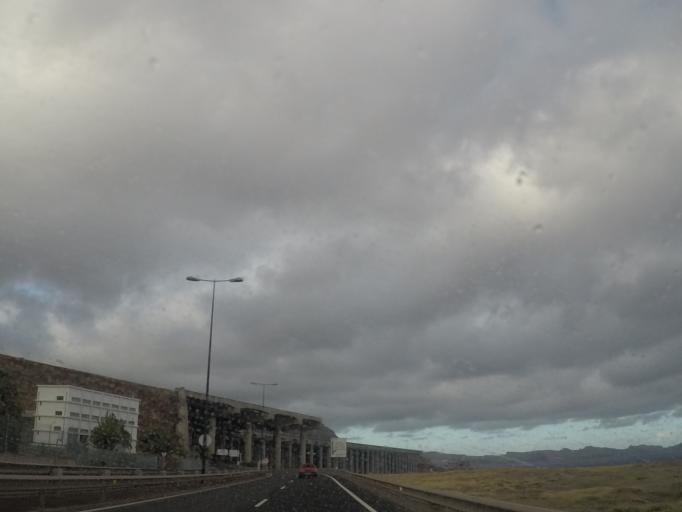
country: PT
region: Madeira
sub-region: Machico
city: Machico
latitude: 32.6965
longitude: -16.7703
